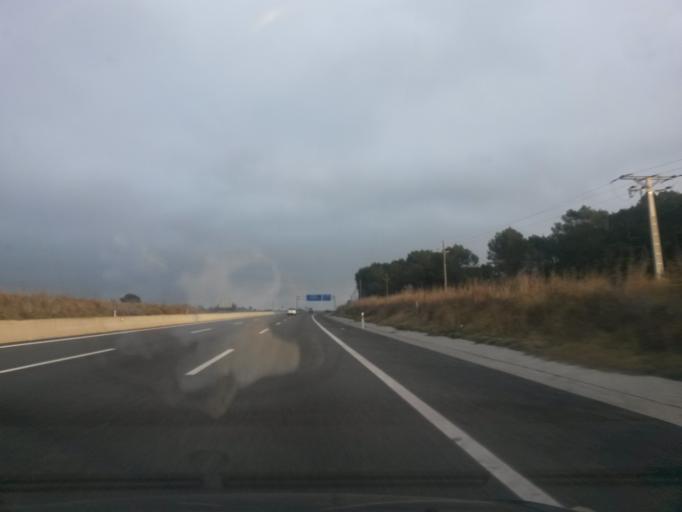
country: ES
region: Catalonia
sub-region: Provincia de Girona
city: Vilademuls
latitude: 42.1190
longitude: 2.9124
